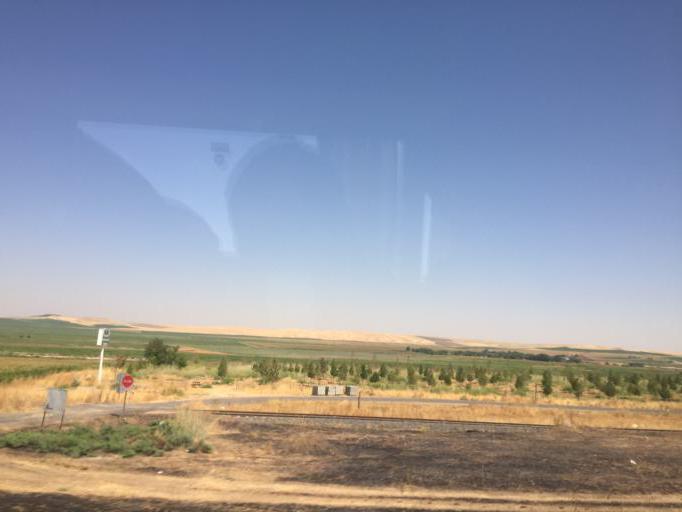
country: TR
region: Diyarbakir
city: Tepe
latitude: 37.8489
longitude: 40.7938
